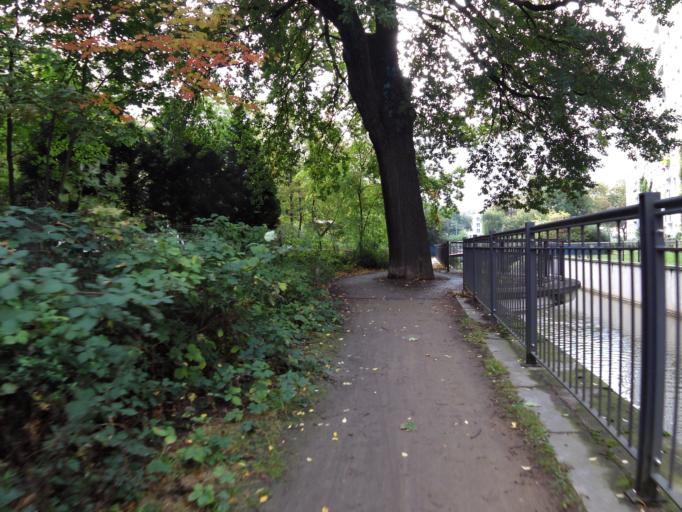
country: DE
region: Saxony
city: Leipzig
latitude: 51.3287
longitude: 12.3693
